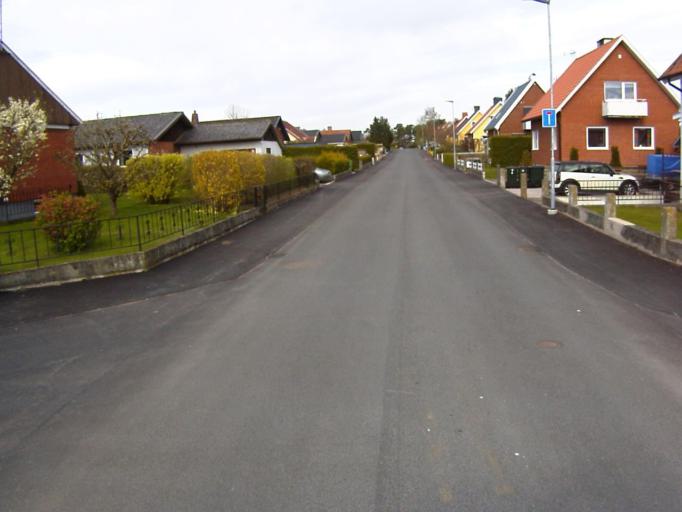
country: SE
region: Skane
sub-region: Kristianstads Kommun
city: Norra Asum
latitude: 55.9923
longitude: 14.1440
